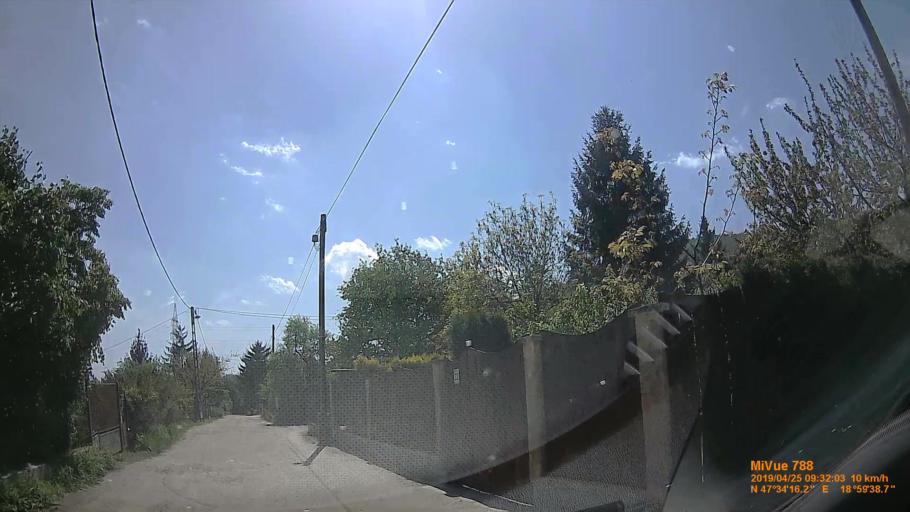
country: HU
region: Pest
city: Urom
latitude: 47.5712
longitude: 18.9941
